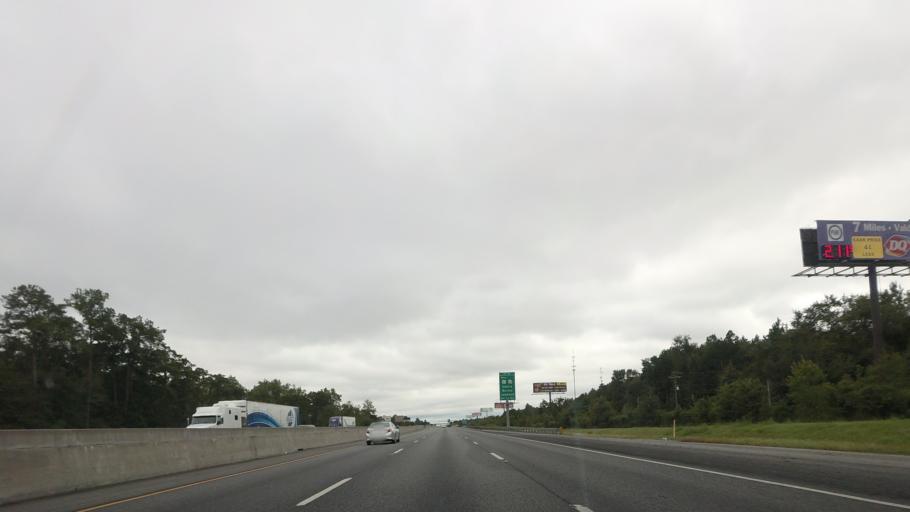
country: US
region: Georgia
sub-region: Lowndes County
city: Hahira
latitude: 31.0022
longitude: -83.3912
